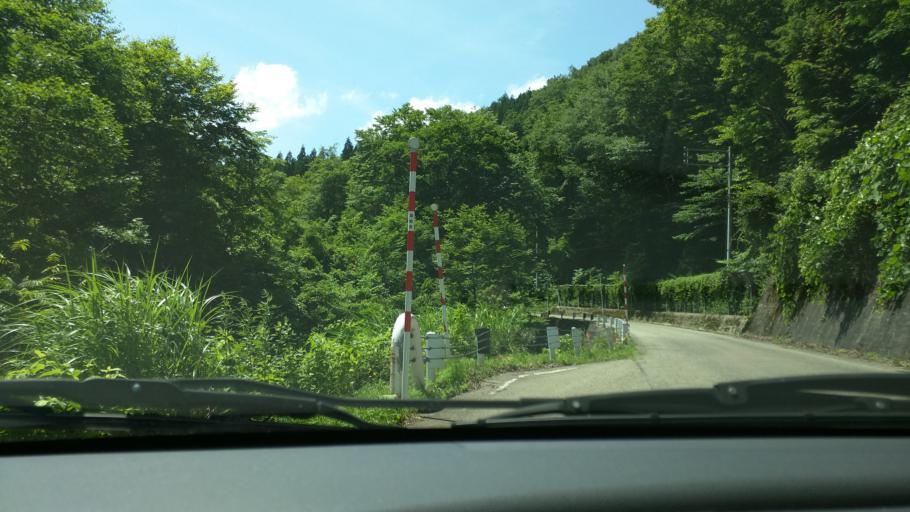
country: JP
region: Fukushima
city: Kitakata
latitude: 37.2559
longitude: 139.7378
